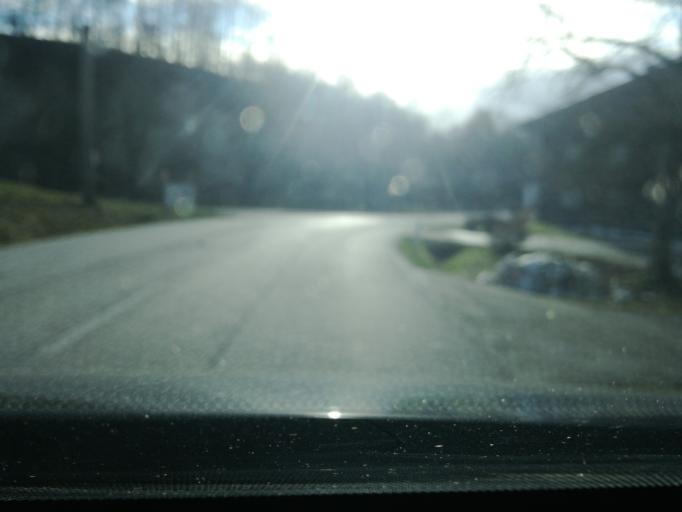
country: AT
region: Upper Austria
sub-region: Politischer Bezirk Ried im Innkreis
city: Waldzell
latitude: 48.1699
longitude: 13.4178
